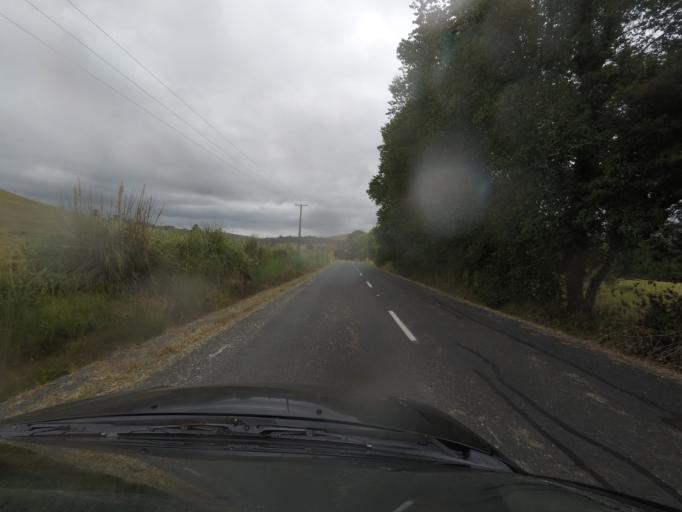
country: NZ
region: Auckland
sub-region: Auckland
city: Warkworth
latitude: -36.2780
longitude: 174.6744
